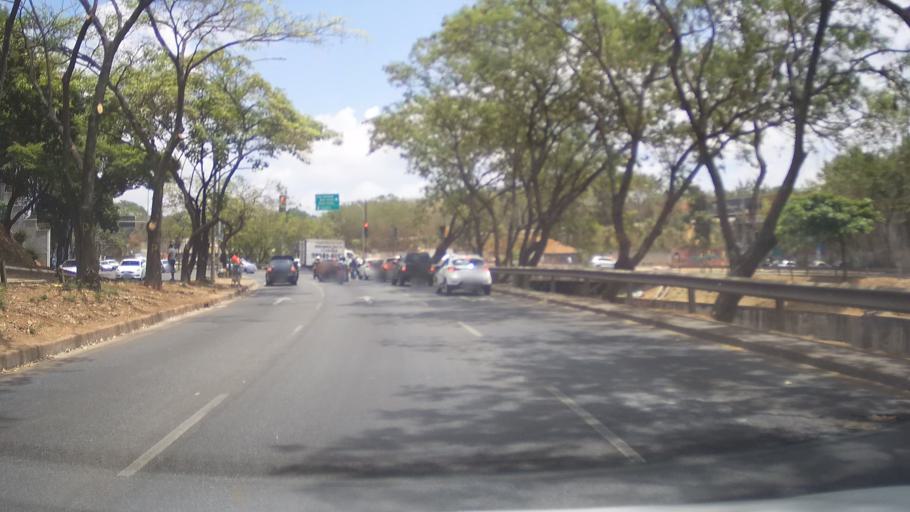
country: BR
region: Minas Gerais
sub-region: Belo Horizonte
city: Belo Horizonte
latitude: -19.9018
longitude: -43.9049
